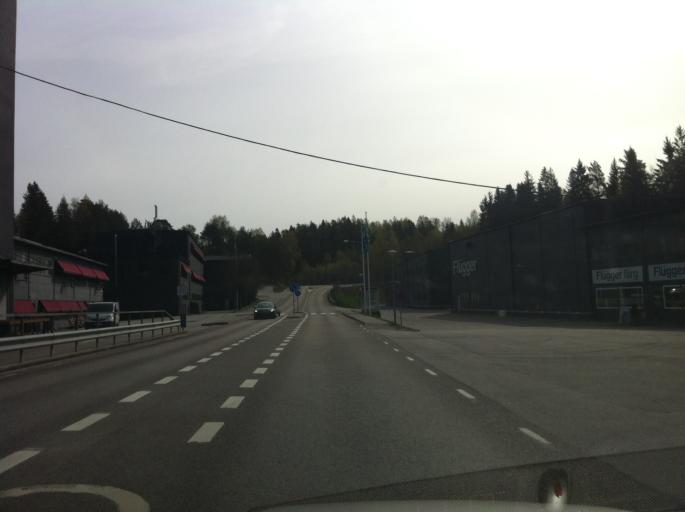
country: SE
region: Vaestra Goetaland
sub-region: Bollebygds Kommun
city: Bollebygd
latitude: 57.6717
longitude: 12.5964
